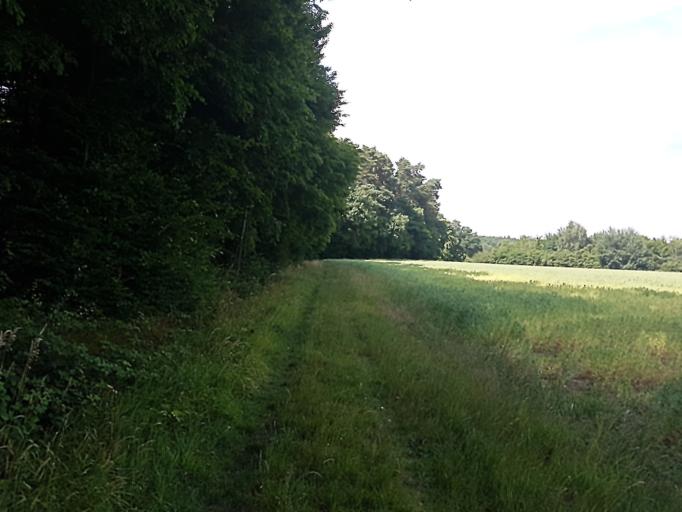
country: DE
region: Bavaria
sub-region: Upper Franconia
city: Litzendorf
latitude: 49.9230
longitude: 10.9907
